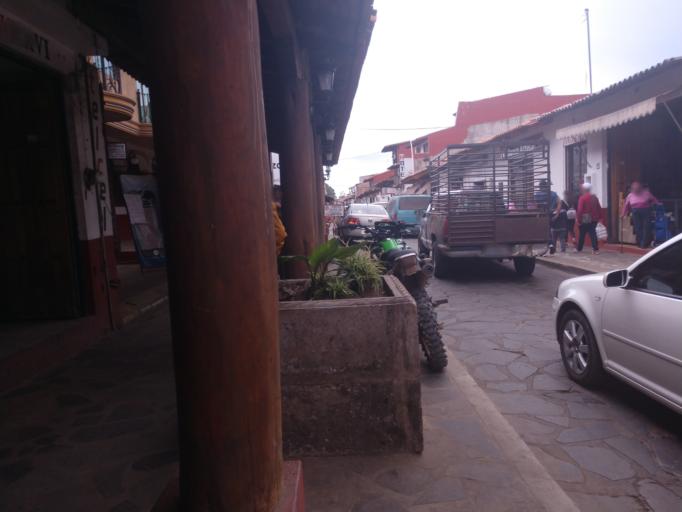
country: MX
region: Jalisco
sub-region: Mazamitla
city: Mazamitla
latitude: 19.9179
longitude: -103.0203
